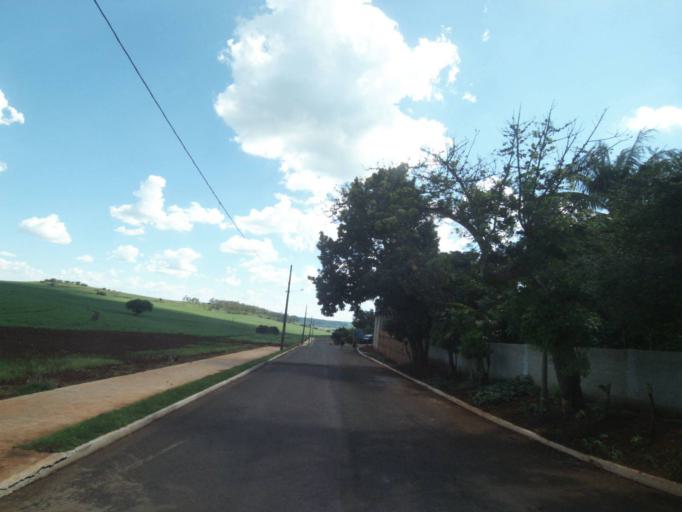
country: BR
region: Parana
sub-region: Sertanopolis
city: Sertanopolis
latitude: -23.0465
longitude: -50.8214
